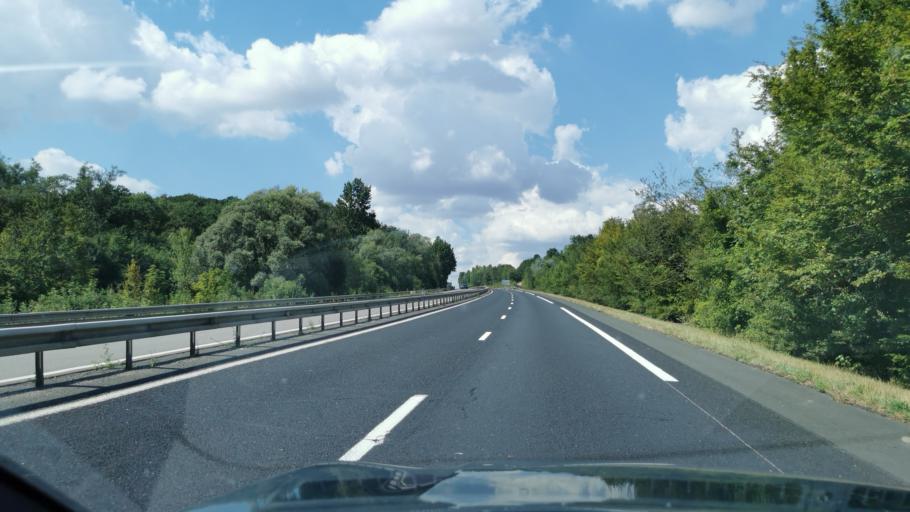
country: FR
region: Lorraine
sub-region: Departement de la Moselle
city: Fontoy
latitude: 49.3763
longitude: 5.9806
